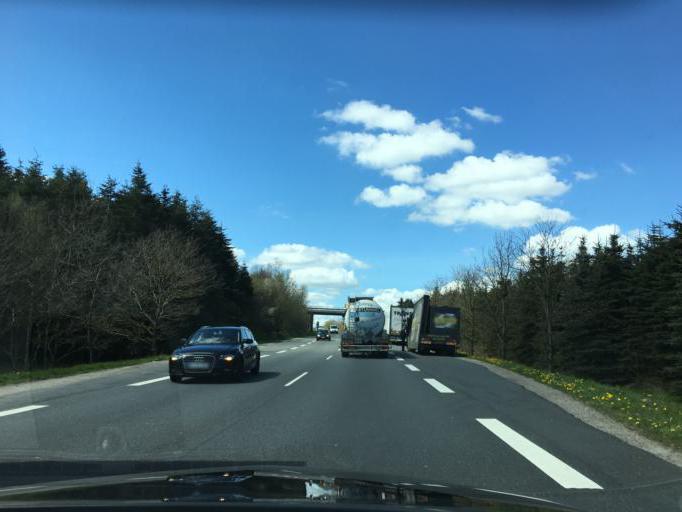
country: DK
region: Central Jutland
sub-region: Hedensted Kommune
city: Hedensted
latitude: 55.8431
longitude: 9.7442
